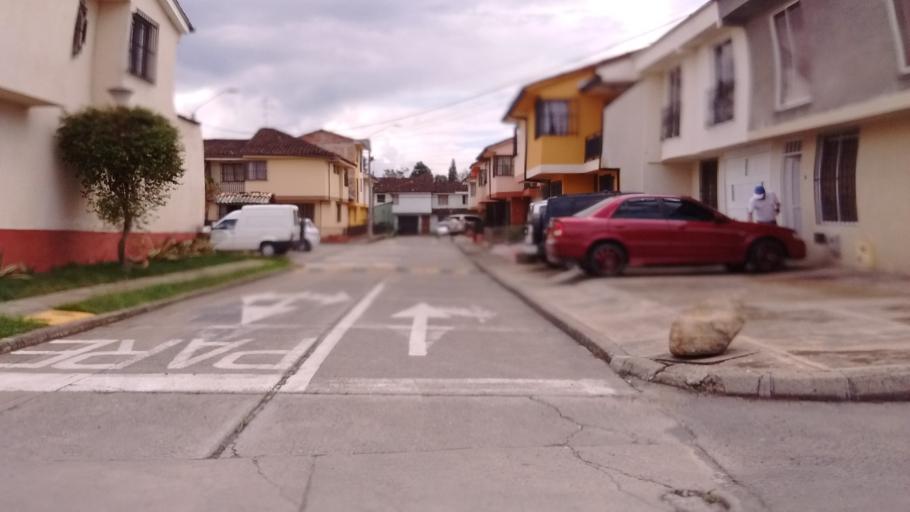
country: CO
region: Cauca
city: Popayan
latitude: 2.4612
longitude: -76.5860
